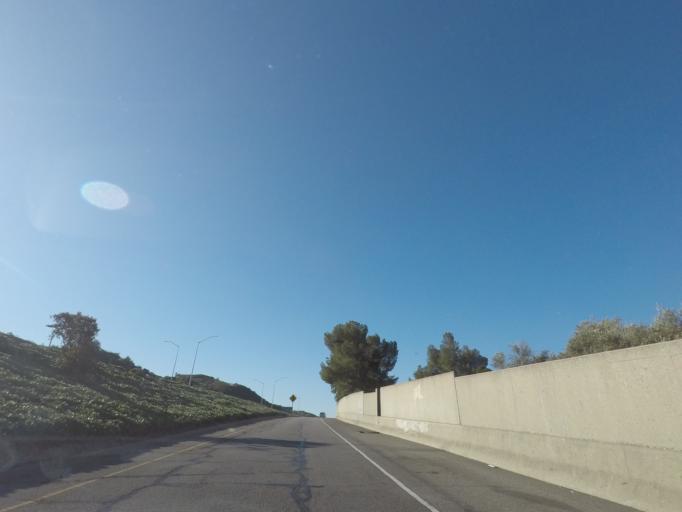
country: US
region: California
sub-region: Los Angeles County
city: La Canada Flintridge
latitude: 34.2036
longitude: -118.2196
